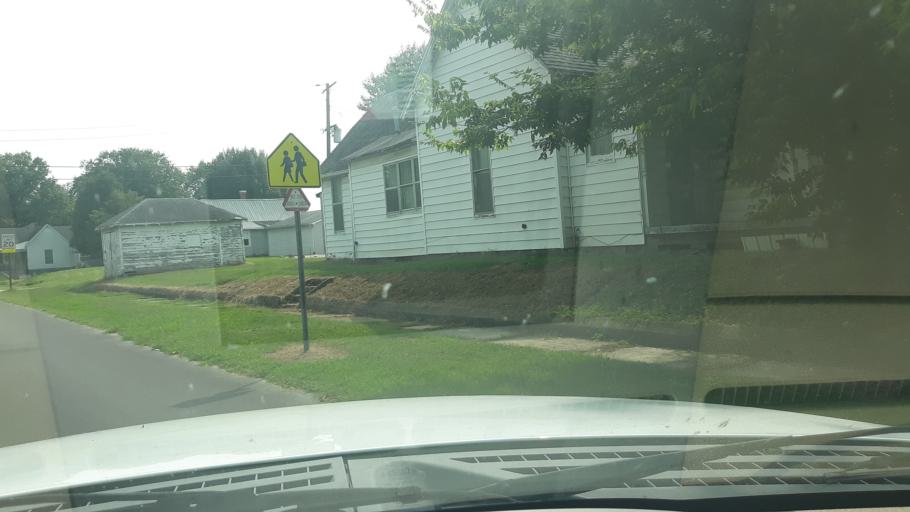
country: US
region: Indiana
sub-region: Gibson County
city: Princeton
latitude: 38.3511
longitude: -87.5632
